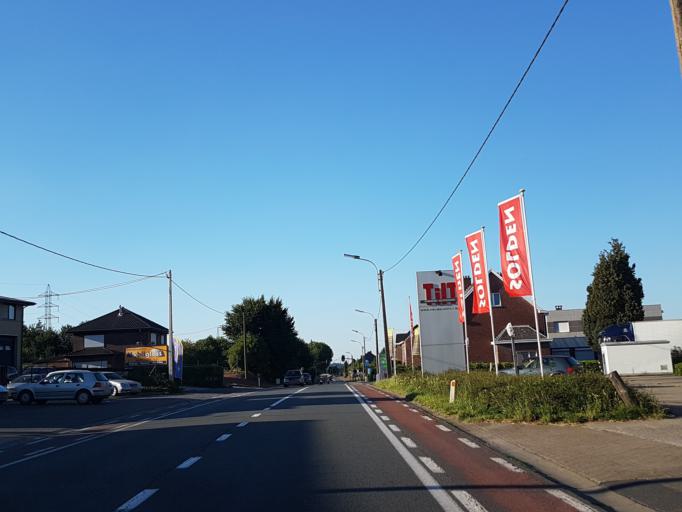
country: BE
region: Flanders
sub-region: Provincie Vlaams-Brabant
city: Ternat
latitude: 50.8536
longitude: 4.1533
